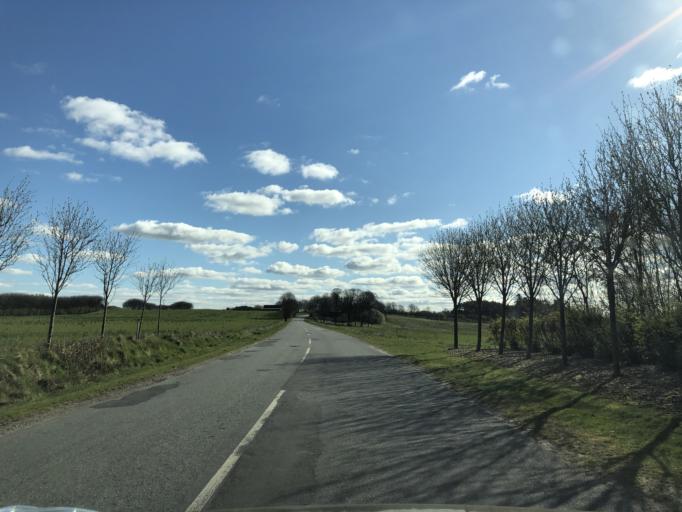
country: DK
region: North Denmark
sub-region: Vesthimmerland Kommune
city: Alestrup
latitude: 56.6058
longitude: 9.5595
